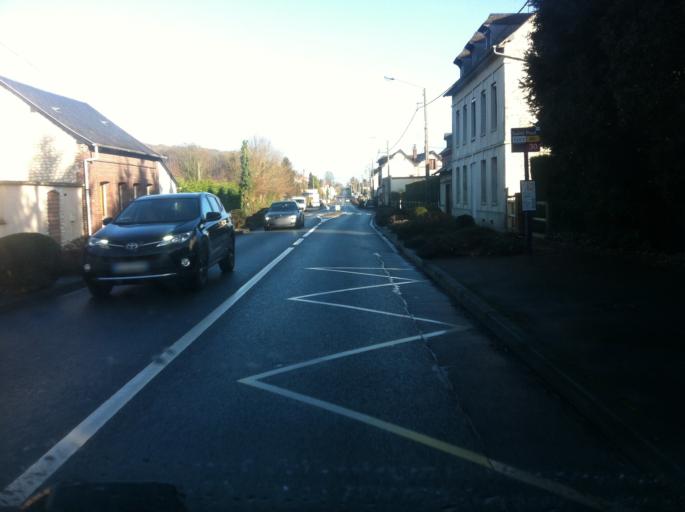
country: FR
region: Haute-Normandie
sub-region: Departement de la Seine-Maritime
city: Duclair
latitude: 49.4692
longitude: 0.8577
